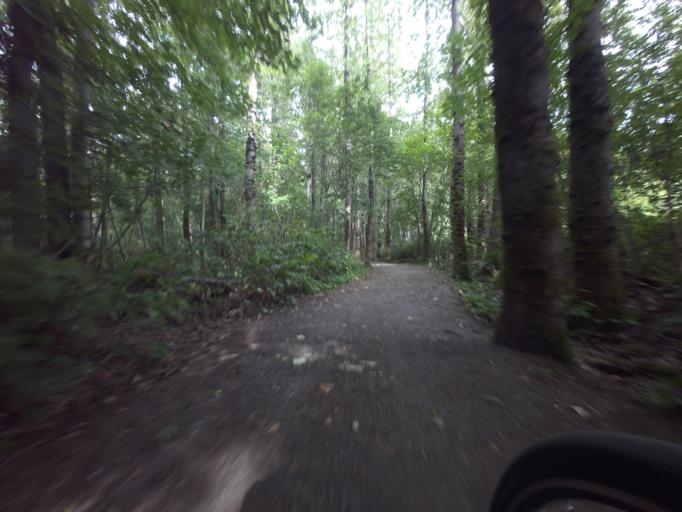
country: CA
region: British Columbia
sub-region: Greater Vancouver Regional District
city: Lions Bay
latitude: 49.7059
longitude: -123.1483
